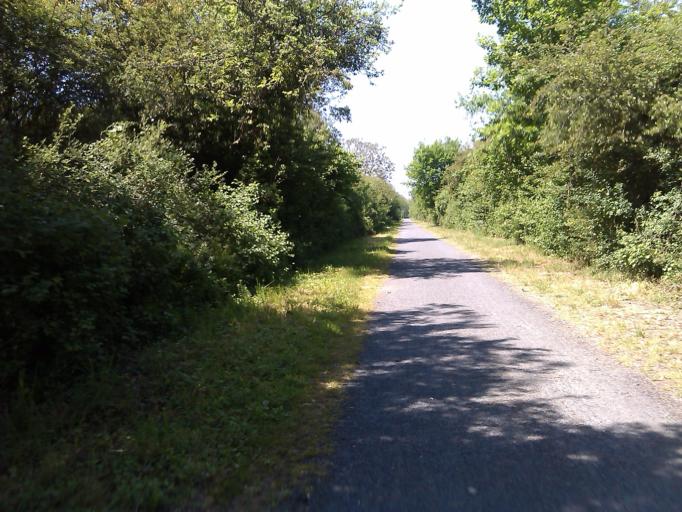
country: FR
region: Centre
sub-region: Departement de l'Indre
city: Saint-Gaultier
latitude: 46.6324
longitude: 1.4137
